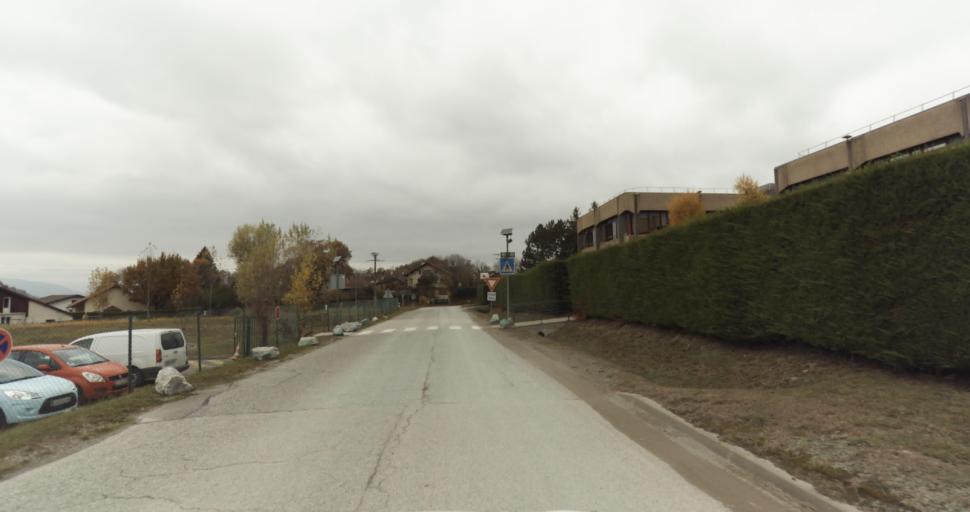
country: FR
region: Rhone-Alpes
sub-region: Departement de la Haute-Savoie
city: Chavanod
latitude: 45.8787
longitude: 6.0422
